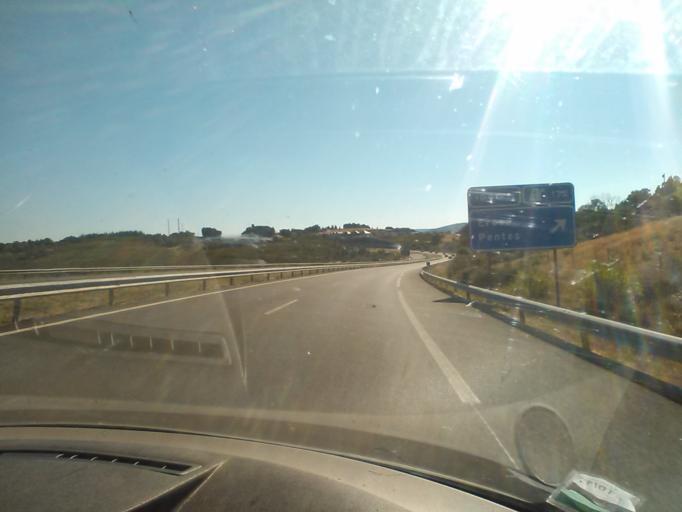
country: ES
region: Galicia
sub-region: Provincia de Ourense
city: Rios
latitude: 42.0348
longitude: -7.1707
